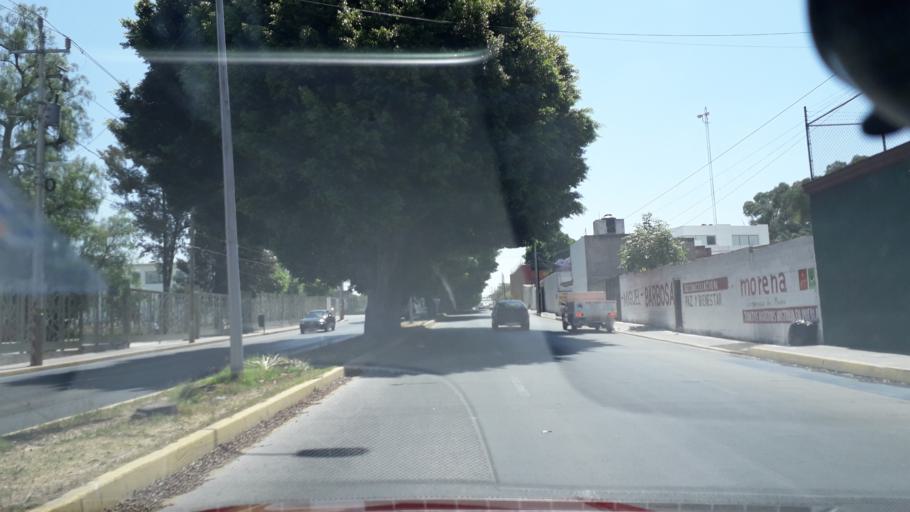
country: MX
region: Puebla
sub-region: Cuautlancingo
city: Sanctorum
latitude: 19.0919
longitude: -98.2334
